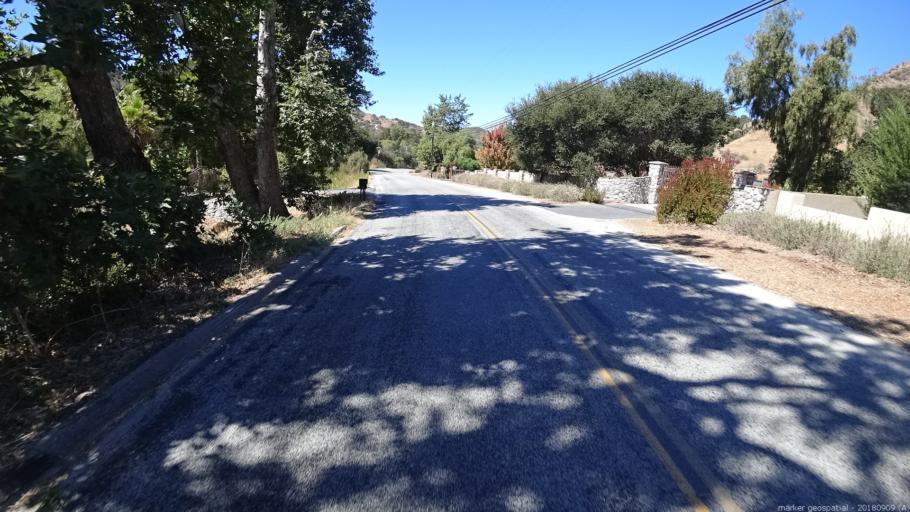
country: US
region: California
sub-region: Monterey County
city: Carmel Valley Village
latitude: 36.5506
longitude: -121.6856
